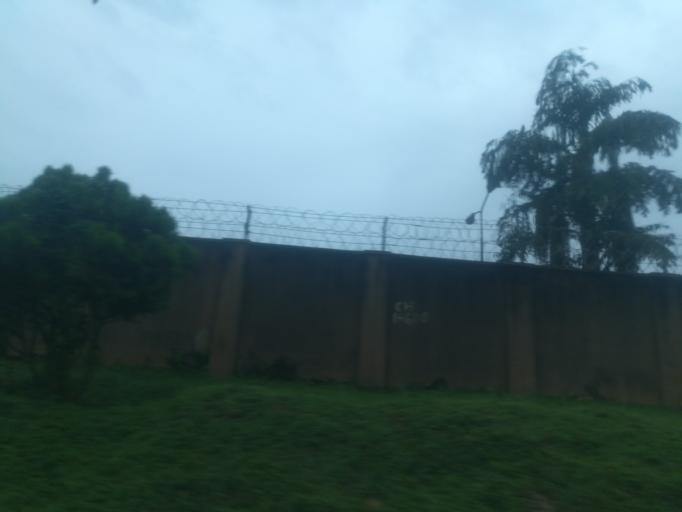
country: NG
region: Oyo
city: Ibadan
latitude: 7.3985
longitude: 3.9659
